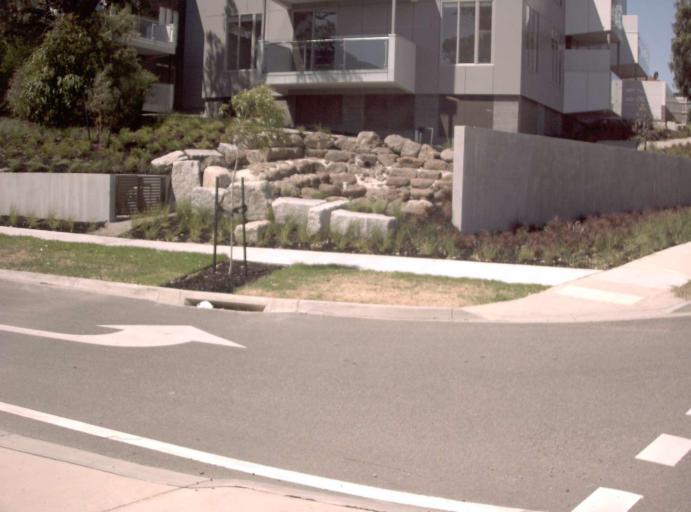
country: AU
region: Victoria
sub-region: Whitehorse
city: Burwood
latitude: -37.8510
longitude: 145.1250
